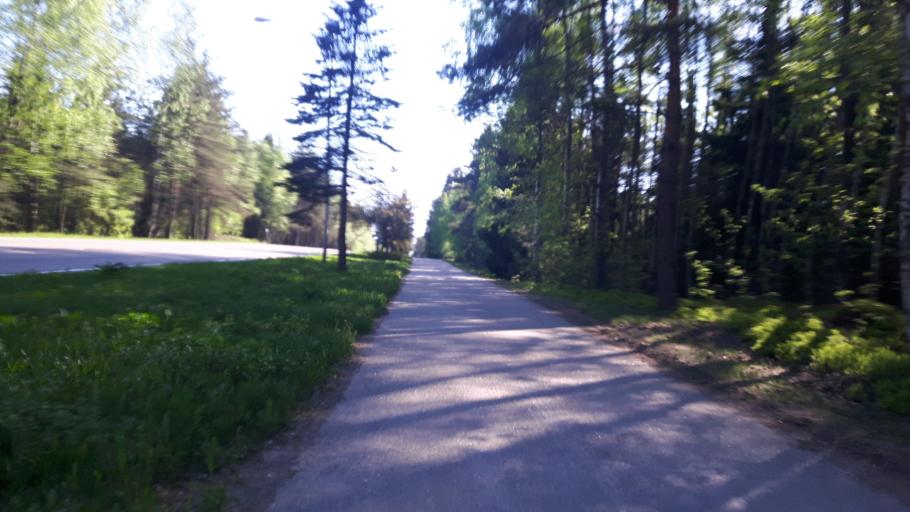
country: FI
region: Kymenlaakso
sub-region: Kotka-Hamina
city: Kotka
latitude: 60.4478
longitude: 26.8938
